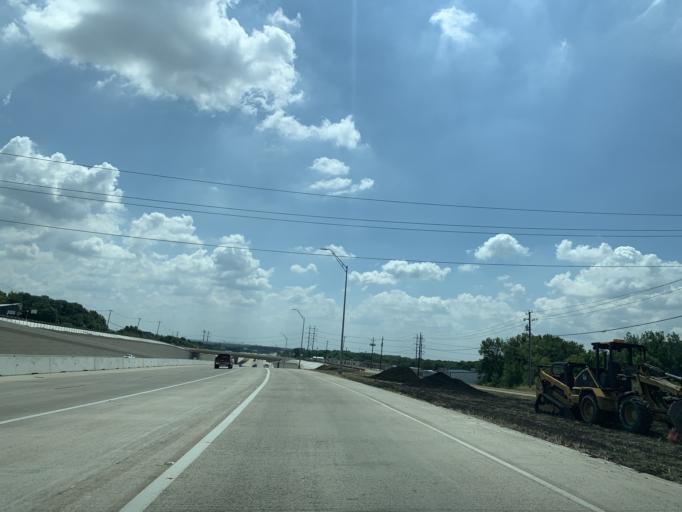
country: US
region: Texas
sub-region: Tarrant County
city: Azle
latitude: 32.8612
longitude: -97.5214
